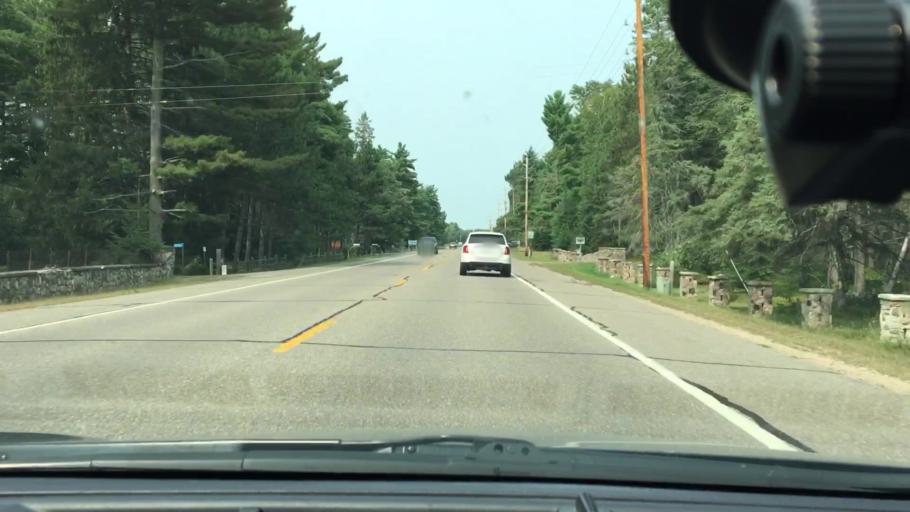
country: US
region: Minnesota
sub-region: Crow Wing County
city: Cross Lake
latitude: 46.5883
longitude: -94.1315
